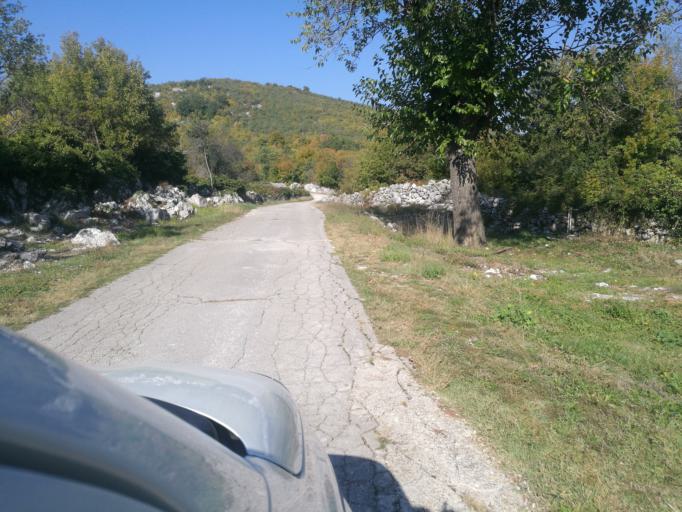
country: HR
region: Splitsko-Dalmatinska
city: Trilj
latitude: 43.5395
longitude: 16.7349
